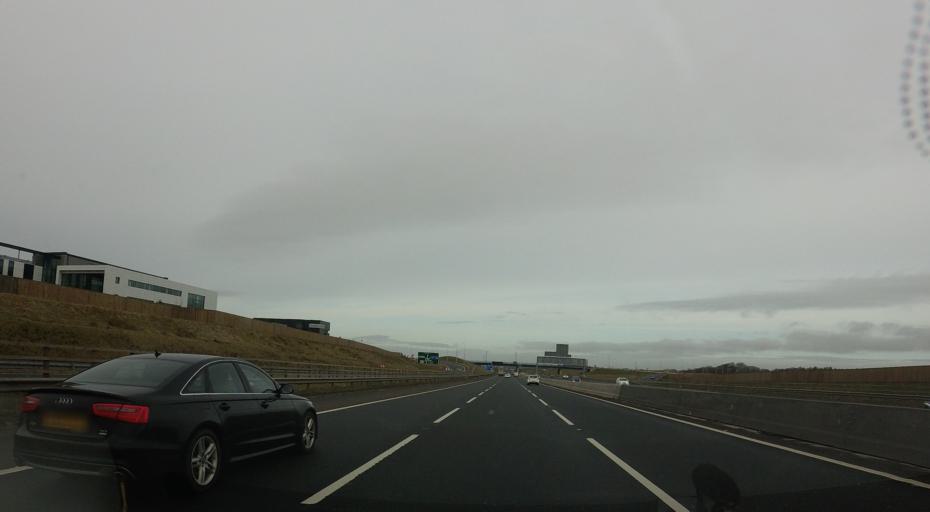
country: GB
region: Scotland
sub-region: North Lanarkshire
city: Holytown
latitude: 55.8359
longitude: -3.9788
